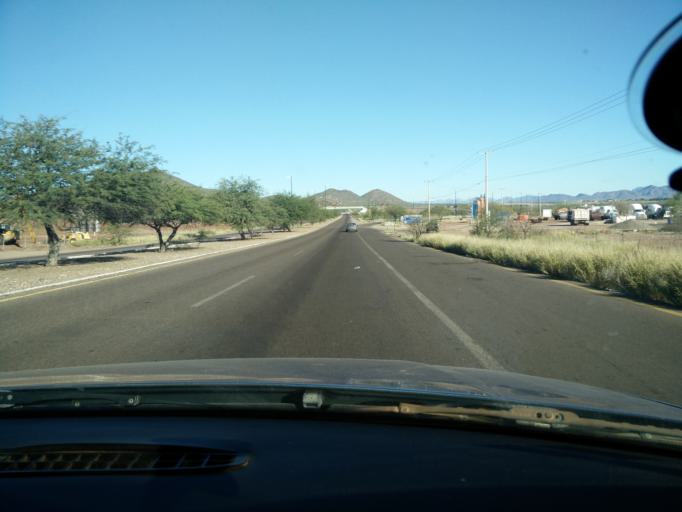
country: MX
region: Sonora
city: Heroica Guaymas
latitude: 27.9823
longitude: -110.9396
